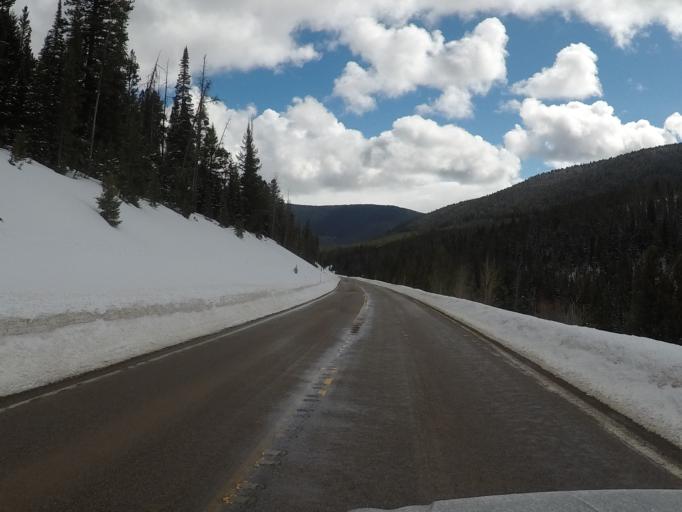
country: US
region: Montana
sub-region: Meagher County
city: White Sulphur Springs
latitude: 46.8073
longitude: -110.7063
